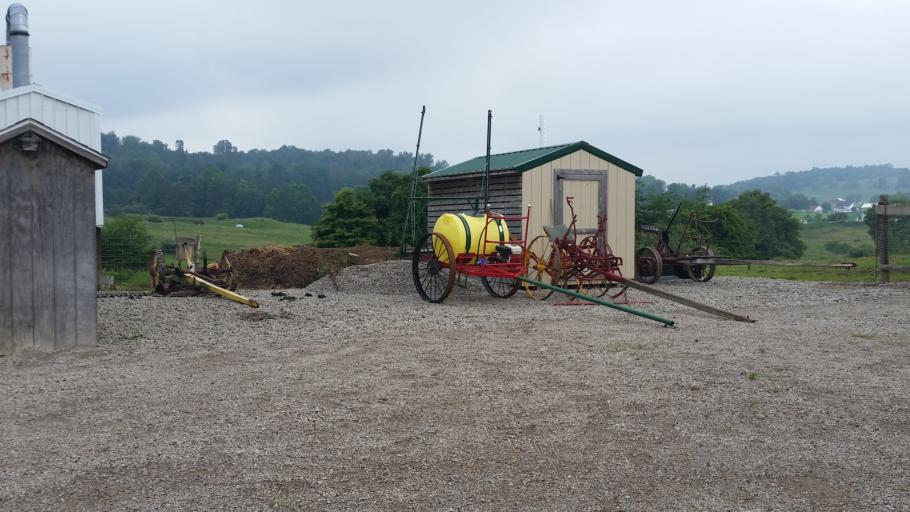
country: US
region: Ohio
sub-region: Gallia County
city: Gallipolis
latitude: 38.7683
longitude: -82.3796
